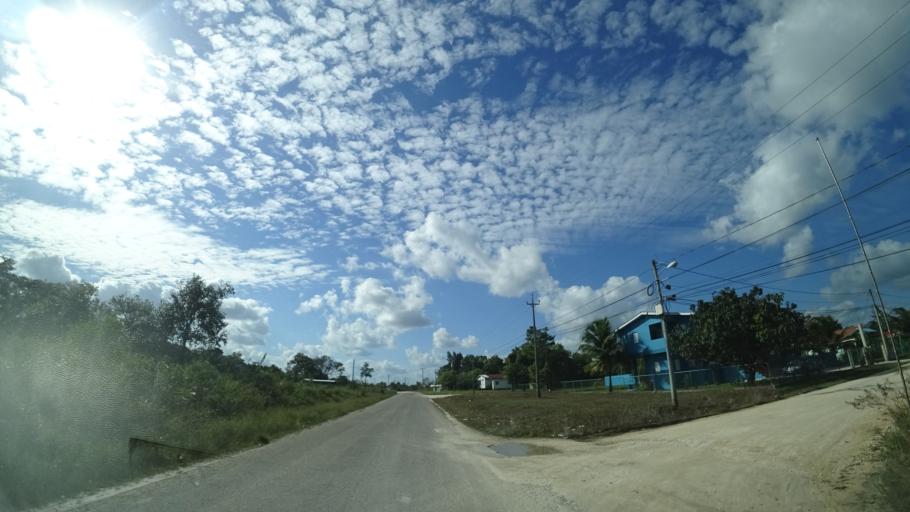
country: BZ
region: Belize
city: Belize City
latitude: 17.5697
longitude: -88.4186
